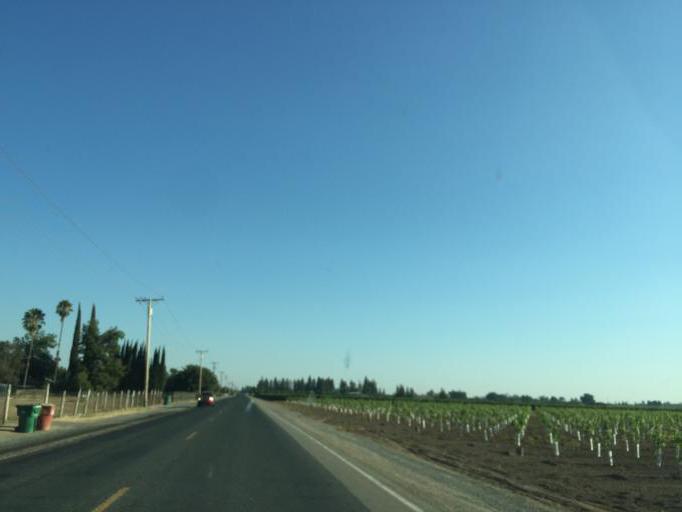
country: US
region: California
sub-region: Tulare County
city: Ivanhoe
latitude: 36.3979
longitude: -119.2784
